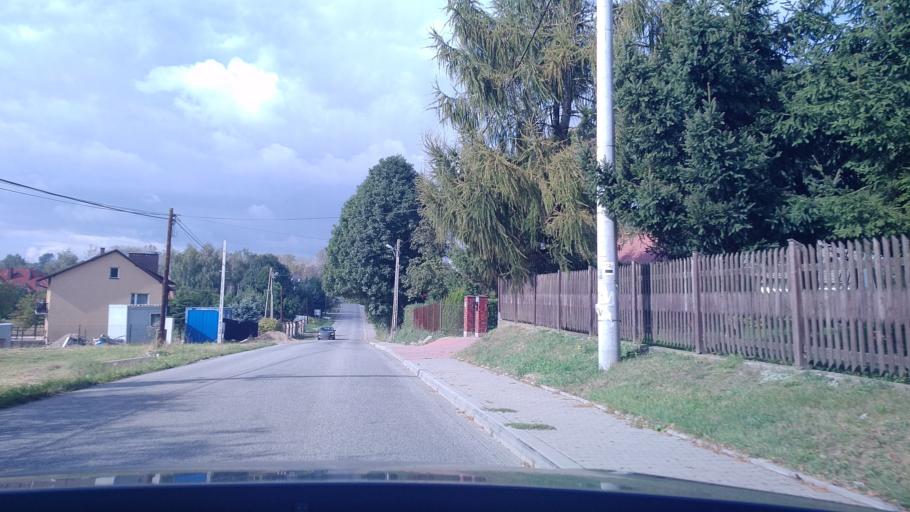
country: PL
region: Lesser Poland Voivodeship
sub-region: Powiat krakowski
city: Modlnica
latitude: 50.1337
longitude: 19.8551
